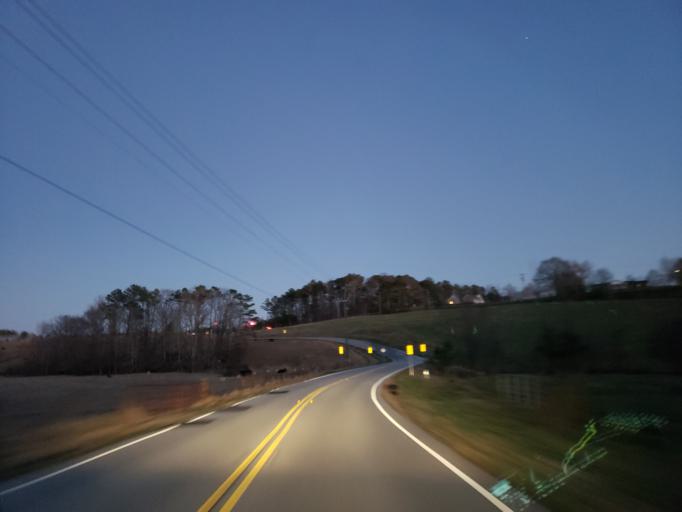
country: US
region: Georgia
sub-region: Bartow County
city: Emerson
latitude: 34.0626
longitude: -84.8100
